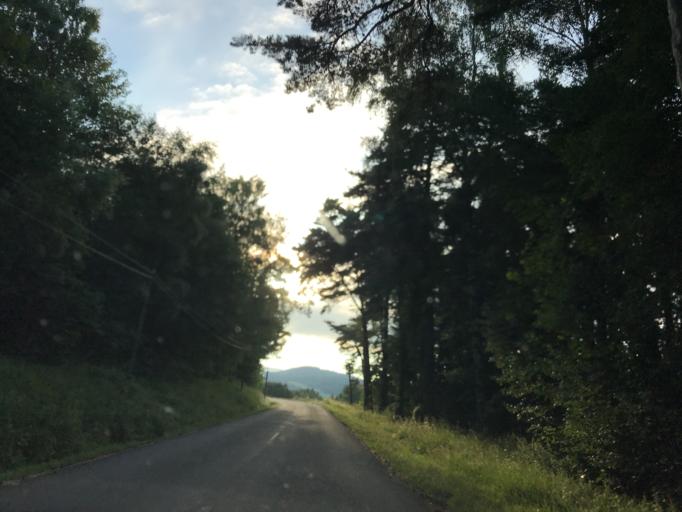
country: FR
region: Rhone-Alpes
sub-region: Departement de la Loire
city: Sail-sous-Couzan
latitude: 45.7417
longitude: 3.8696
